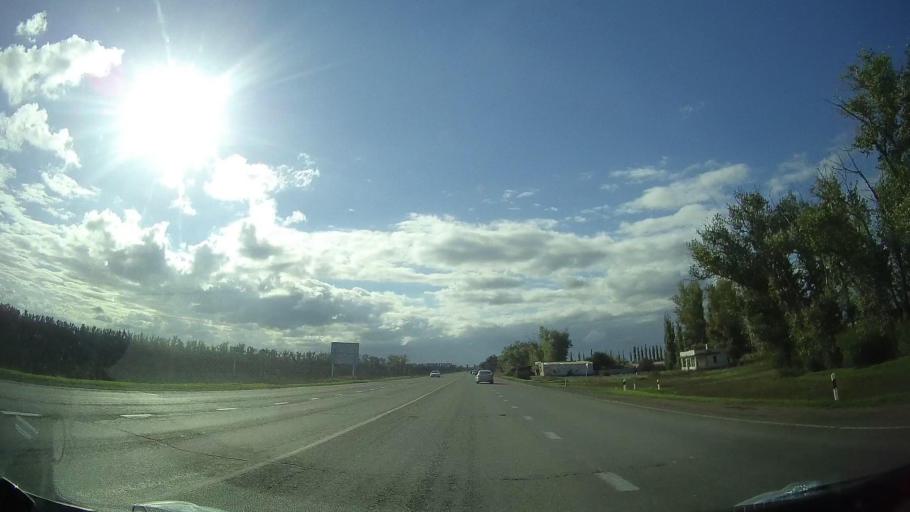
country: RU
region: Rostov
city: Tselina
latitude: 46.5328
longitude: 40.9782
